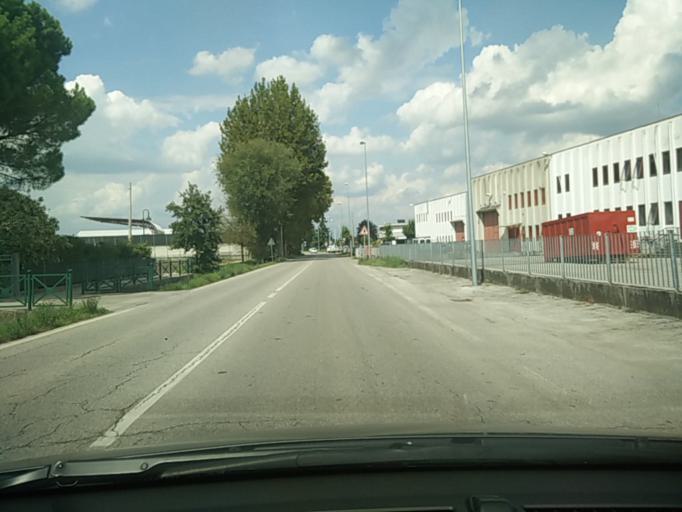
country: IT
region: Veneto
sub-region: Provincia di Treviso
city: Lancenigo-Villorba
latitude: 45.7304
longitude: 12.2398
